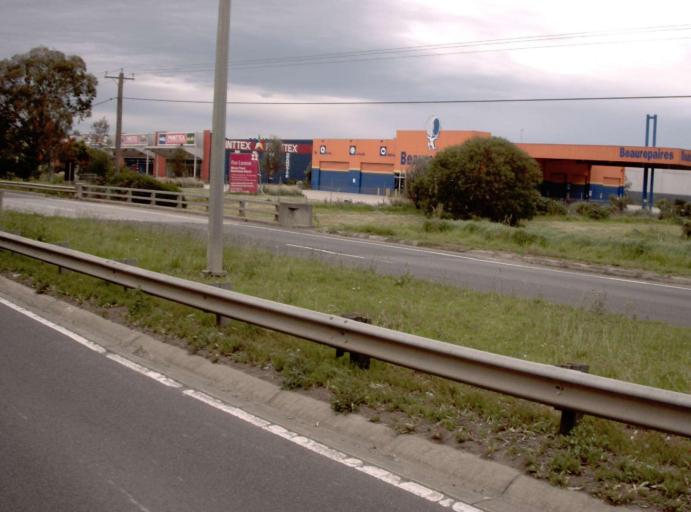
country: AU
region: Victoria
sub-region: Casey
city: Hampton Park
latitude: -38.0196
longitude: 145.2373
